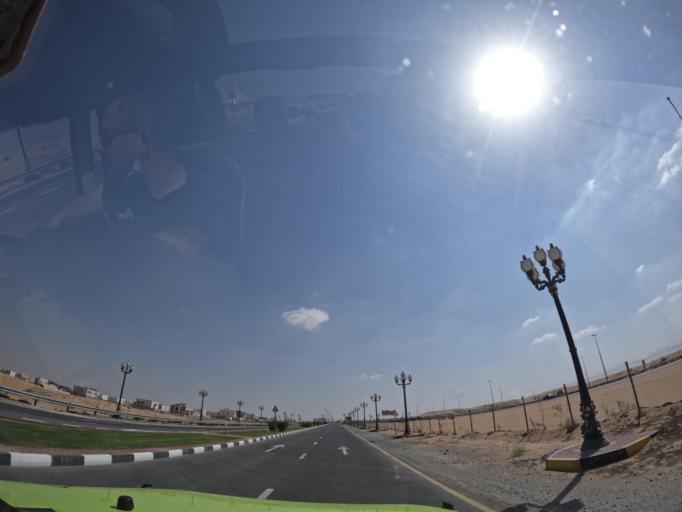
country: AE
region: Ash Shariqah
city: Sharjah
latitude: 25.2352
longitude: 55.5772
